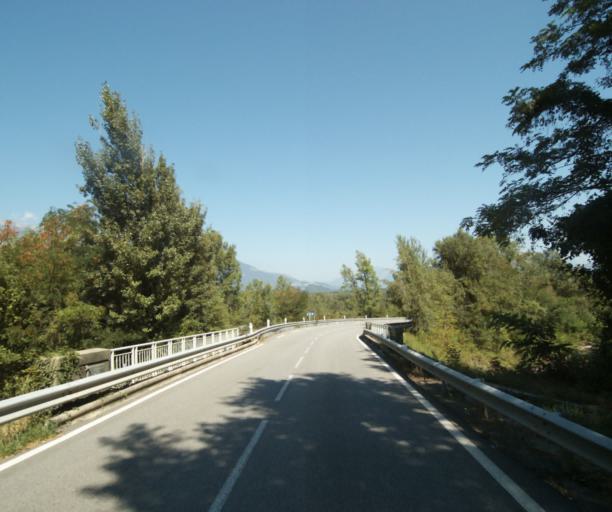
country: FR
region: Rhone-Alpes
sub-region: Departement de l'Isere
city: Saint-Georges-de-Commiers
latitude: 45.0491
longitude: 5.7091
